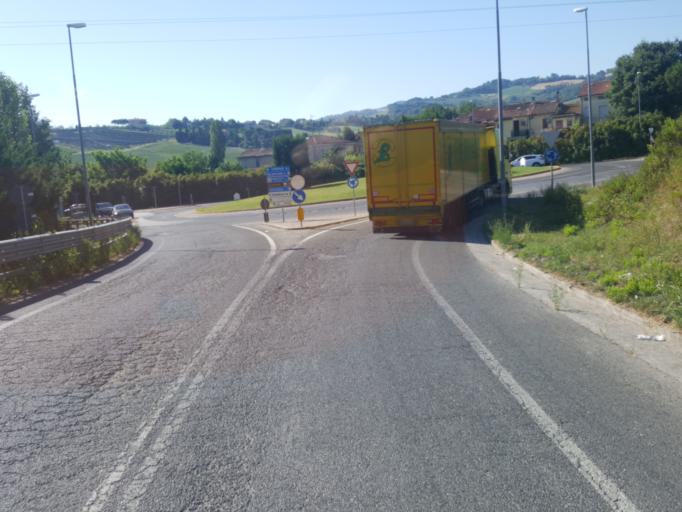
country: IT
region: The Marches
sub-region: Provincia di Pesaro e Urbino
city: Cappone
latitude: 43.8367
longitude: 12.7502
